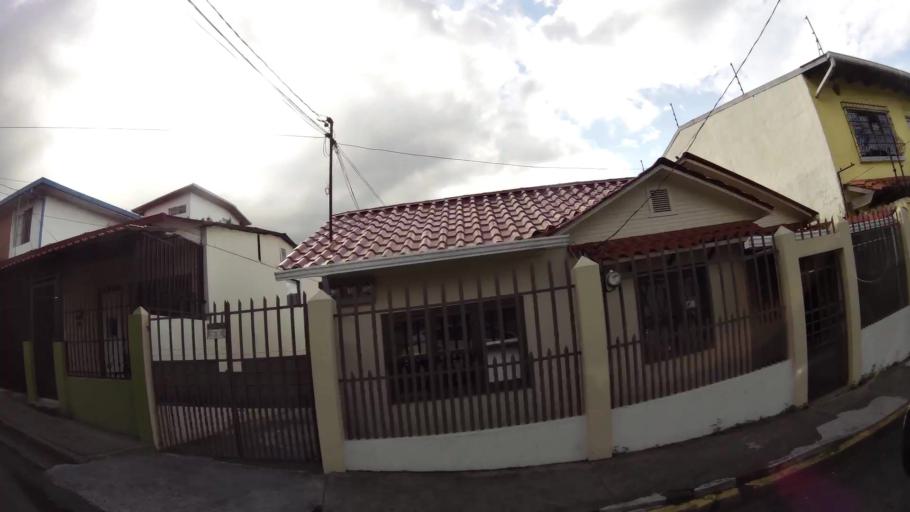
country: CR
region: San Jose
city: Escazu
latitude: 9.9190
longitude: -84.1401
